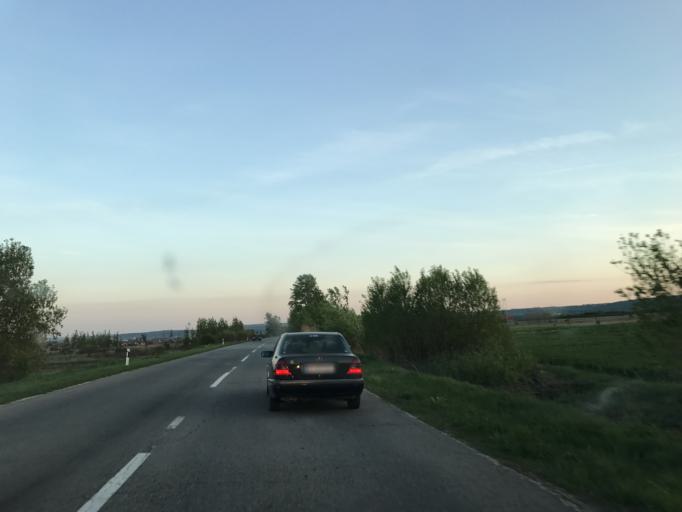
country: RS
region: Central Serbia
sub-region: Borski Okrug
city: Negotin
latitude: 44.2578
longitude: 22.5190
